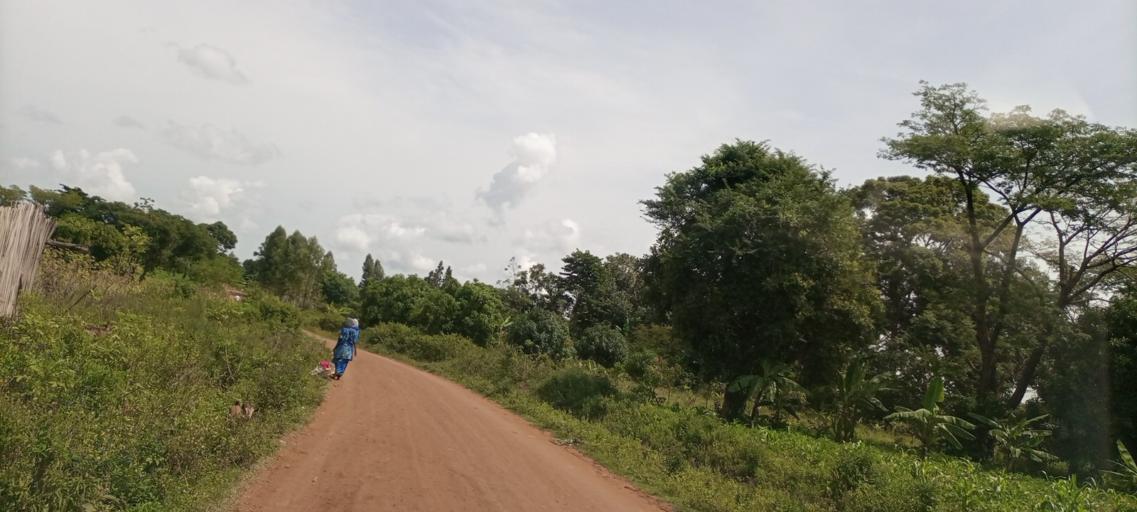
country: UG
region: Eastern Region
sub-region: Budaka District
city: Budaka
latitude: 1.1727
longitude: 33.9323
